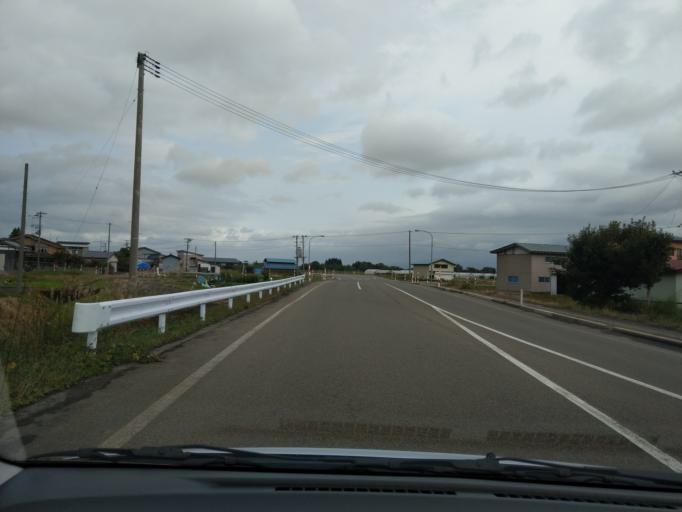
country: JP
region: Akita
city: Omagari
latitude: 39.3808
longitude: 140.4861
